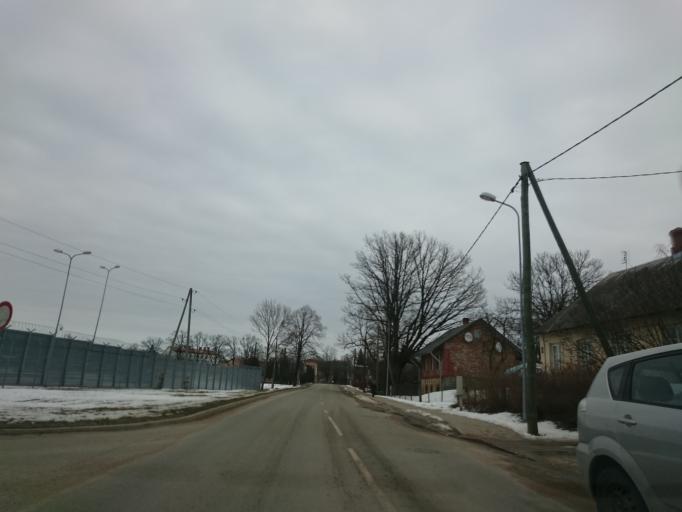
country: LV
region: Cesu Rajons
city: Cesis
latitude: 57.3066
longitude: 25.2599
